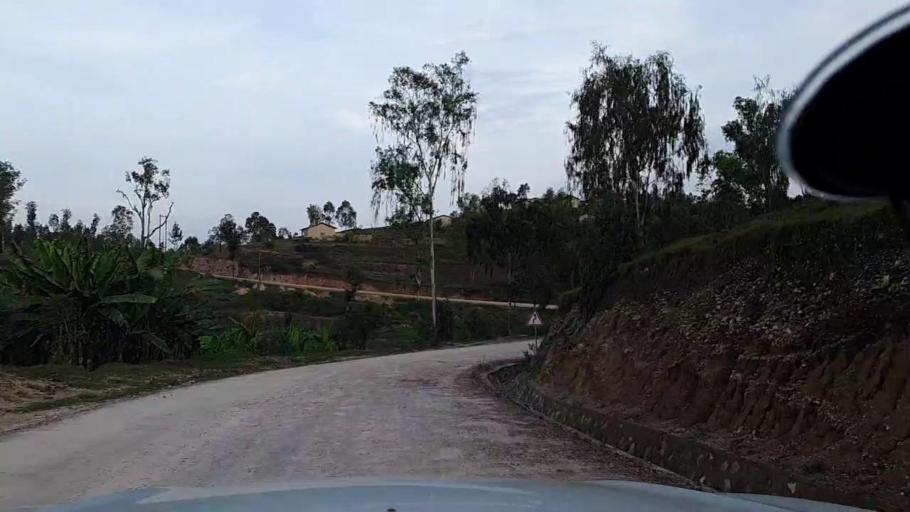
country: RW
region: Southern Province
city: Nyanza
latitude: -2.2256
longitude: 29.6527
